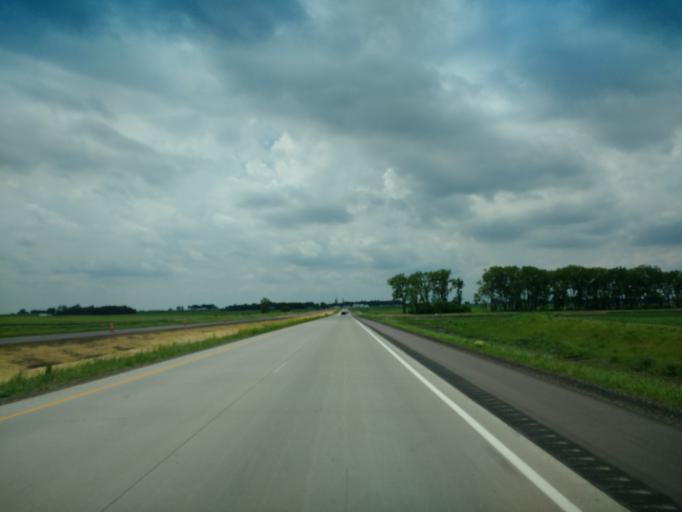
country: US
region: Minnesota
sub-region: Cottonwood County
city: Mountain Lake
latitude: 43.9145
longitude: -95.0156
